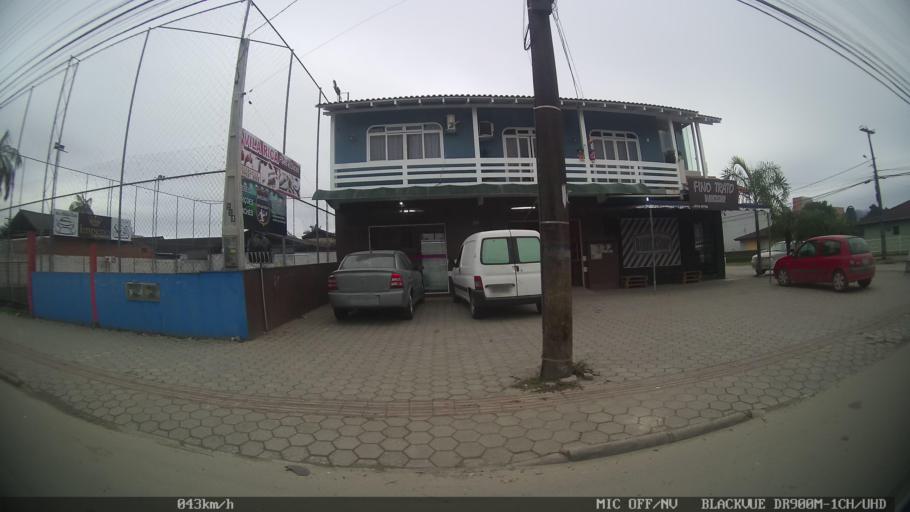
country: BR
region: Santa Catarina
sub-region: Joinville
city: Joinville
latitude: -26.2953
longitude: -48.9000
